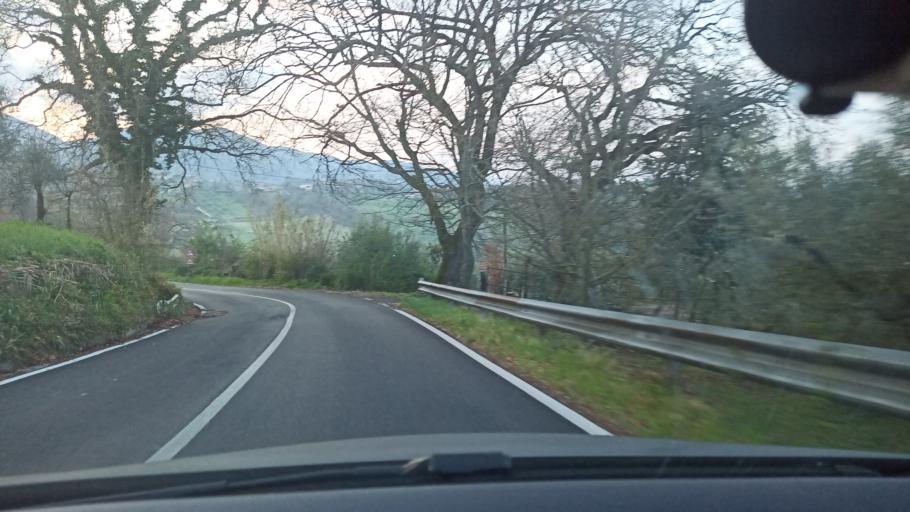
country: IT
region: Latium
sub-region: Provincia di Rieti
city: Torri in Sabina
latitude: 42.3296
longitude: 12.6441
